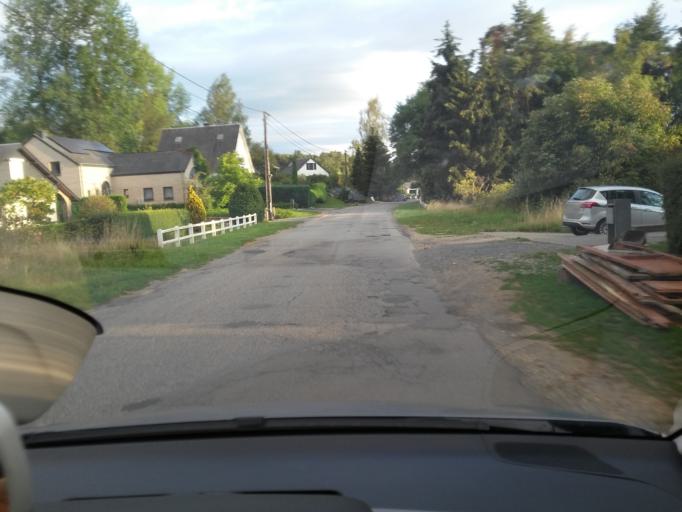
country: BE
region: Wallonia
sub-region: Province du Luxembourg
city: Arlon
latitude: 49.7012
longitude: 5.8127
